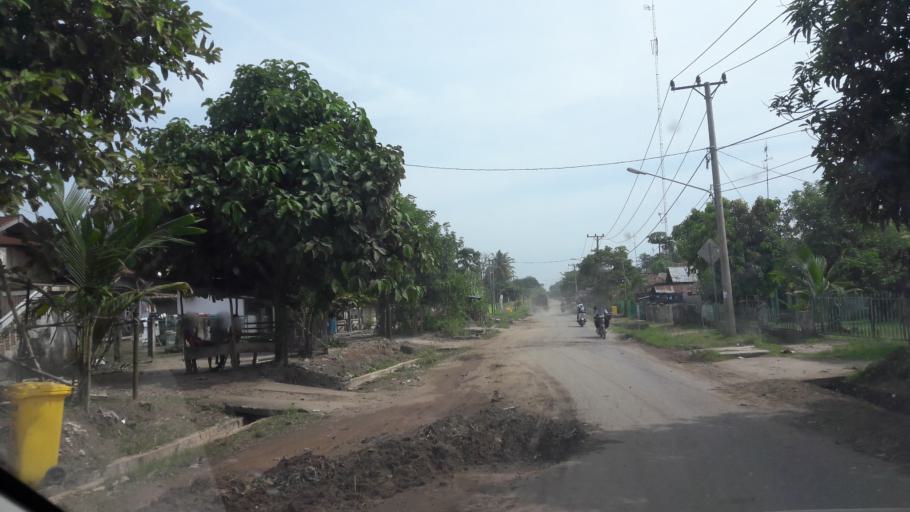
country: ID
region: South Sumatra
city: Gunungmenang
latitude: -3.2623
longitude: 104.1562
